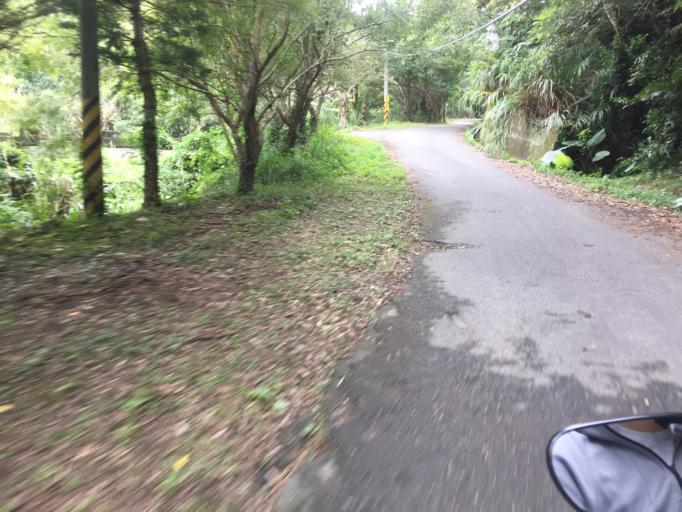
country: TW
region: Taiwan
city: Daxi
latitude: 24.7874
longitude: 121.1609
